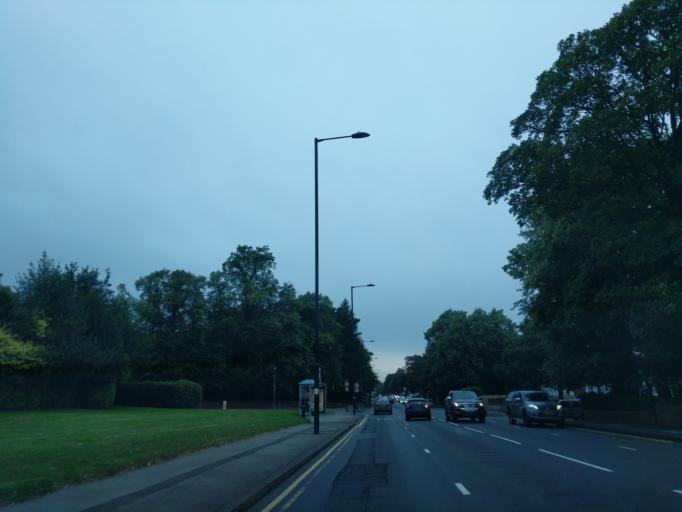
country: GB
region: England
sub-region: Sandwell
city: Smethwick
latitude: 52.4726
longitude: -1.9516
